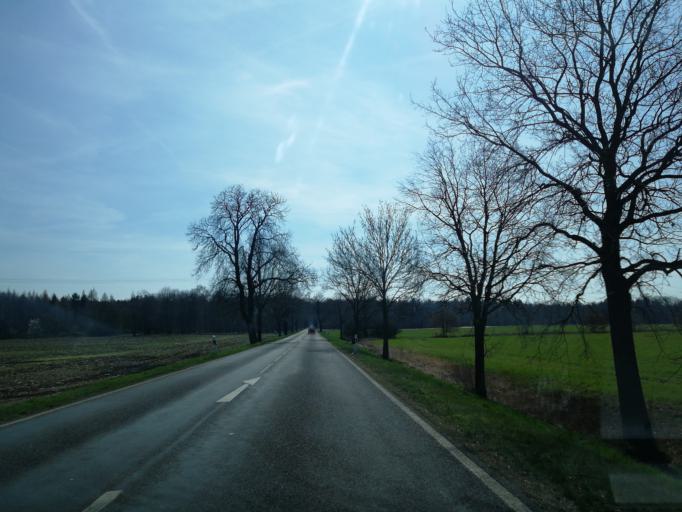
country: DE
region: Brandenburg
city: Altdobern
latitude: 51.6641
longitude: 14.0361
